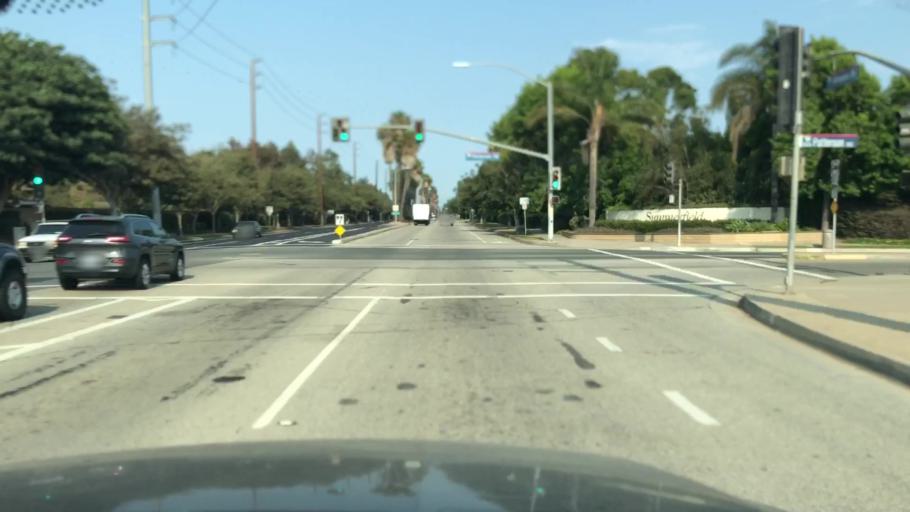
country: US
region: California
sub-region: Ventura County
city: Oxnard
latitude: 34.2193
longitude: -119.2073
